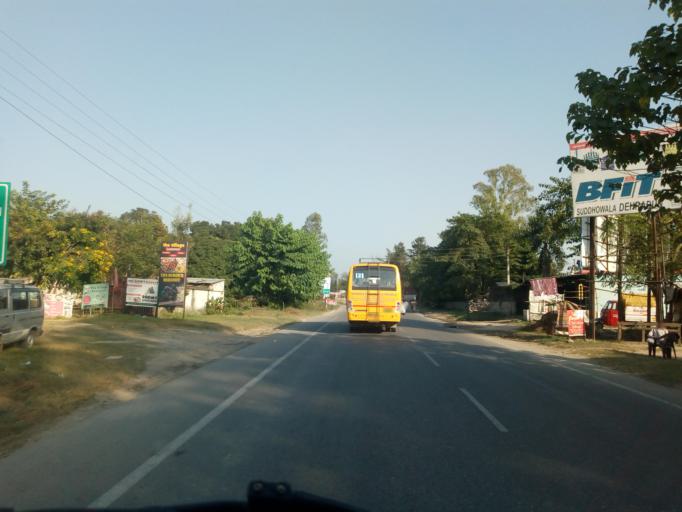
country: IN
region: Uttarakhand
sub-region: Dehradun
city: Dehradun
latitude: 30.3445
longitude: 77.9122
